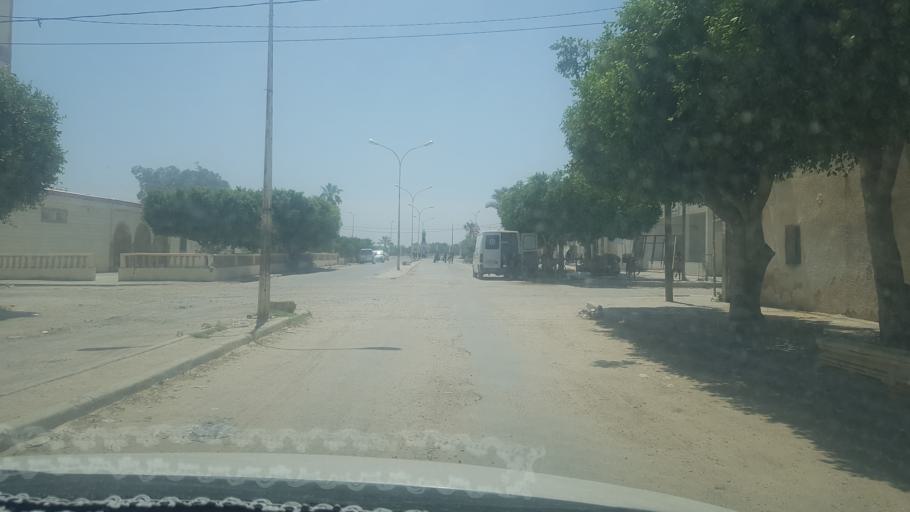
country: TN
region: Al Qayrawan
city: Kairouan
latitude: 35.6175
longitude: 9.9263
